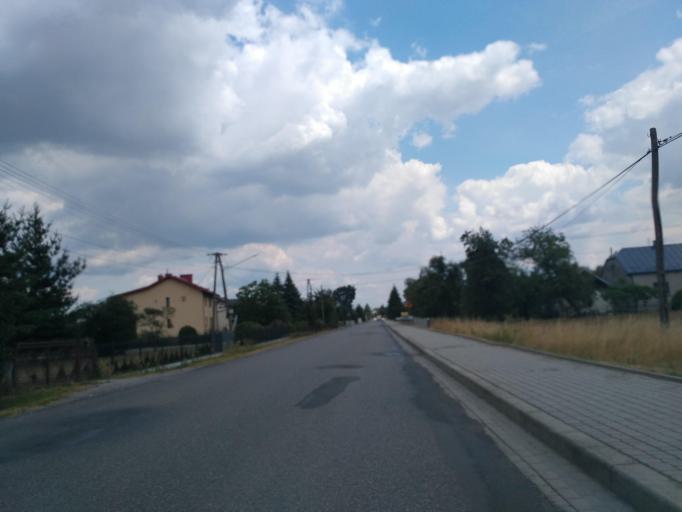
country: PL
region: Subcarpathian Voivodeship
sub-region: Powiat debicki
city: Pilzno
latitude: 50.0402
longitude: 21.3269
